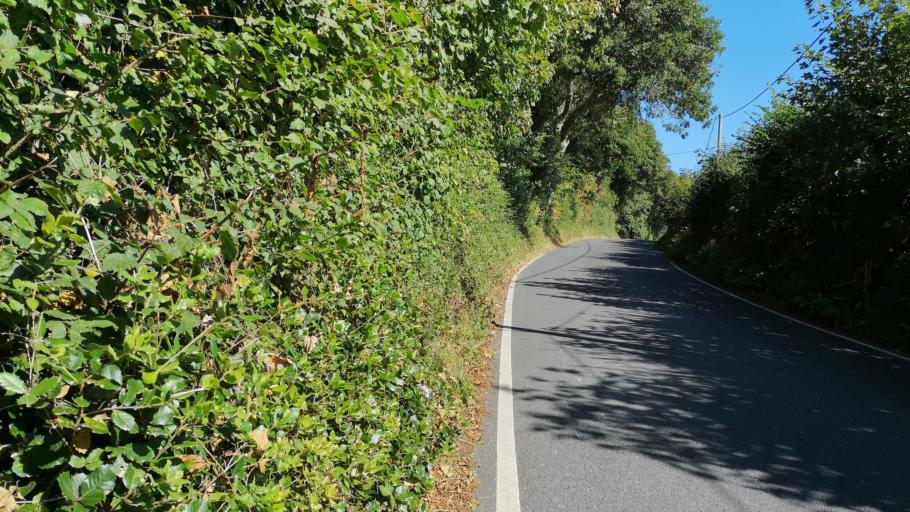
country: GB
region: England
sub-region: Isle of Wight
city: Totland
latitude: 50.6724
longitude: -1.5413
